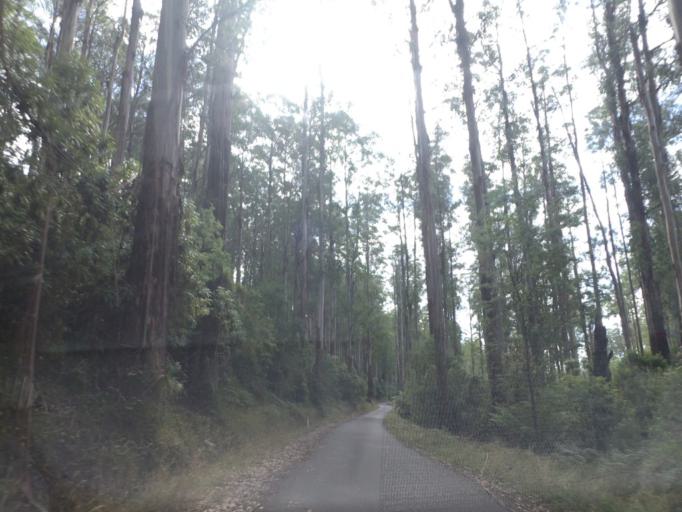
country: AU
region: Victoria
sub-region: Yarra Ranges
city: Millgrove
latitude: -37.5960
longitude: 145.7013
